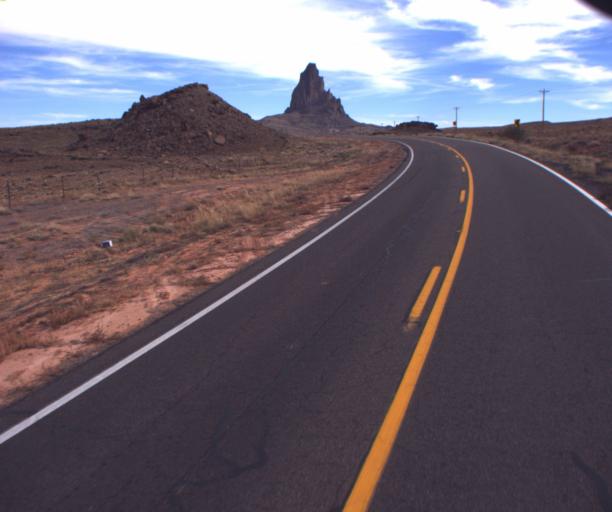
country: US
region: Arizona
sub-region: Navajo County
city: Kayenta
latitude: 36.8405
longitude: -110.2645
